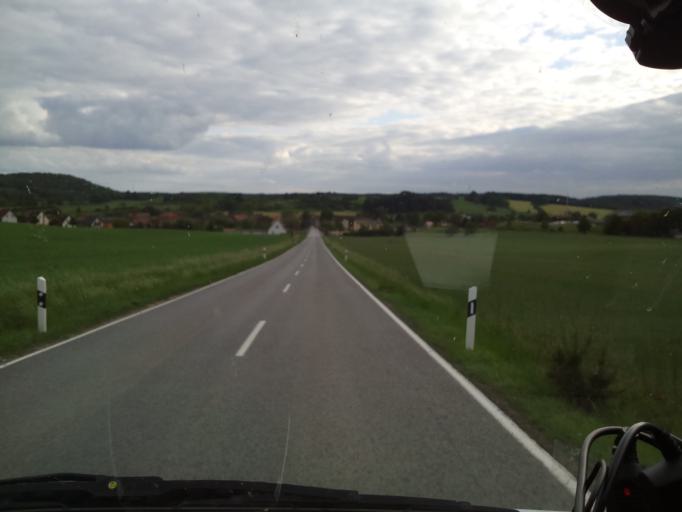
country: DE
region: Thuringia
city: Hellingen
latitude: 50.2583
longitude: 10.6872
